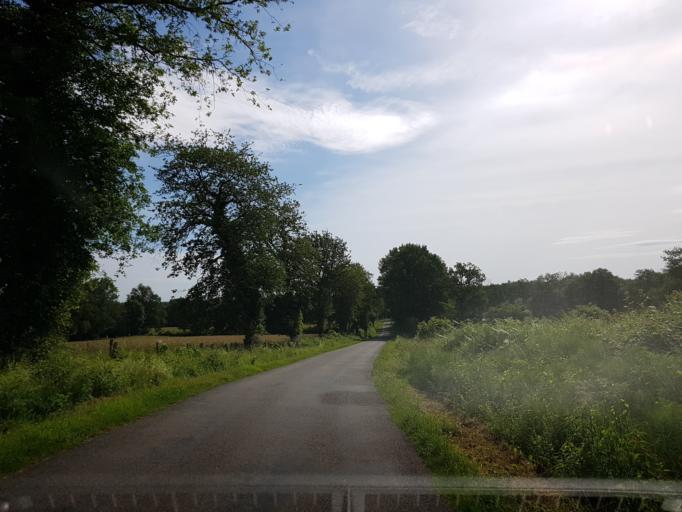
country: FR
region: Poitou-Charentes
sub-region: Departement de la Charente
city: Exideuil
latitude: 45.9192
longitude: 0.7025
